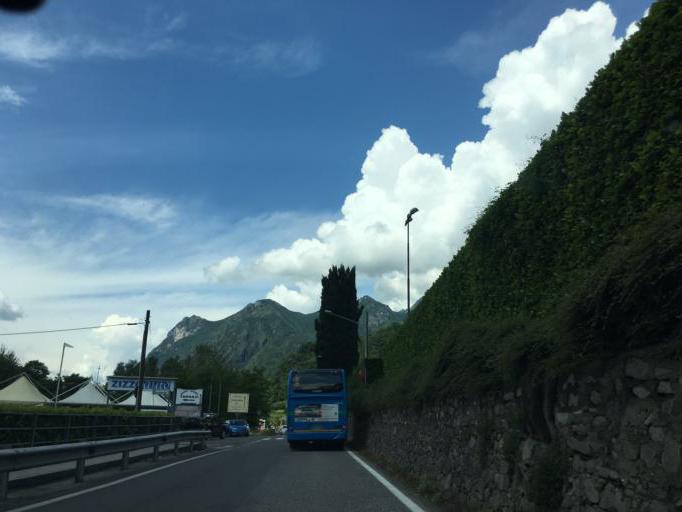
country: IT
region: Lombardy
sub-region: Provincia di Como
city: Carlazzo
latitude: 46.0428
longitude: 9.1599
